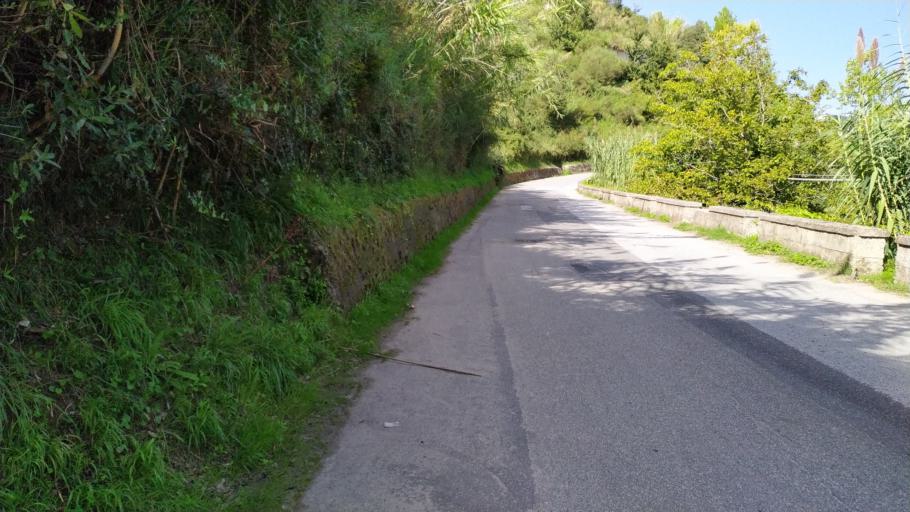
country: IT
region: Sicily
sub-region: Messina
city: Rometta
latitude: 38.1634
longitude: 15.4174
